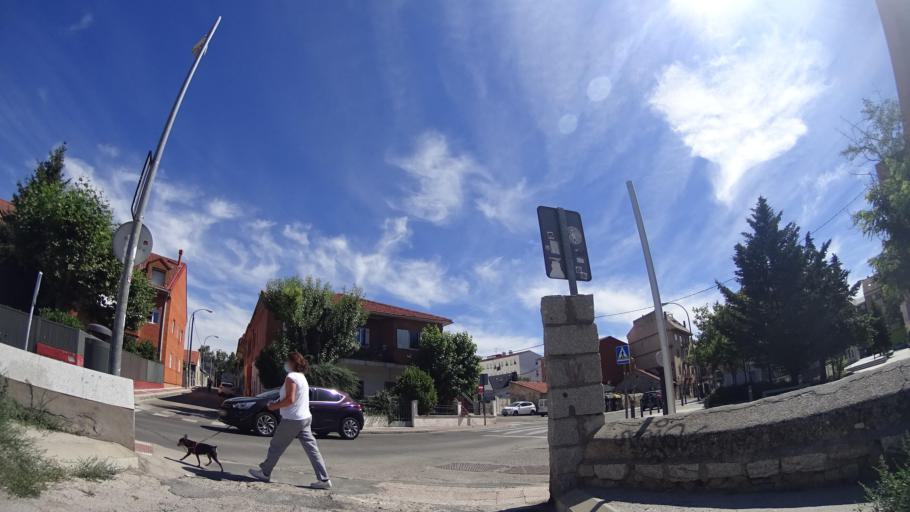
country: ES
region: Madrid
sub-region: Provincia de Madrid
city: Collado-Villalba
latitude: 40.6287
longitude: -4.0098
